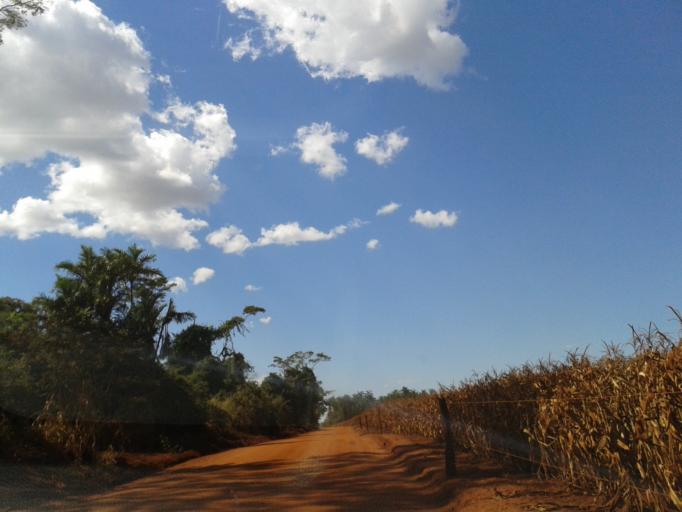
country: BR
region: Minas Gerais
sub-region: Capinopolis
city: Capinopolis
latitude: -18.6188
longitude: -49.4774
